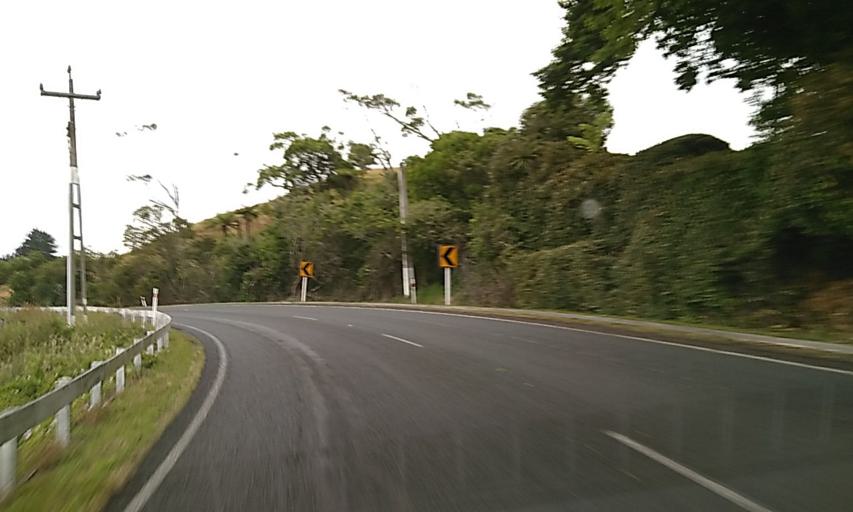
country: NZ
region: Auckland
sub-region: Auckland
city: Pukekohe East
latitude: -37.3100
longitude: 174.9376
